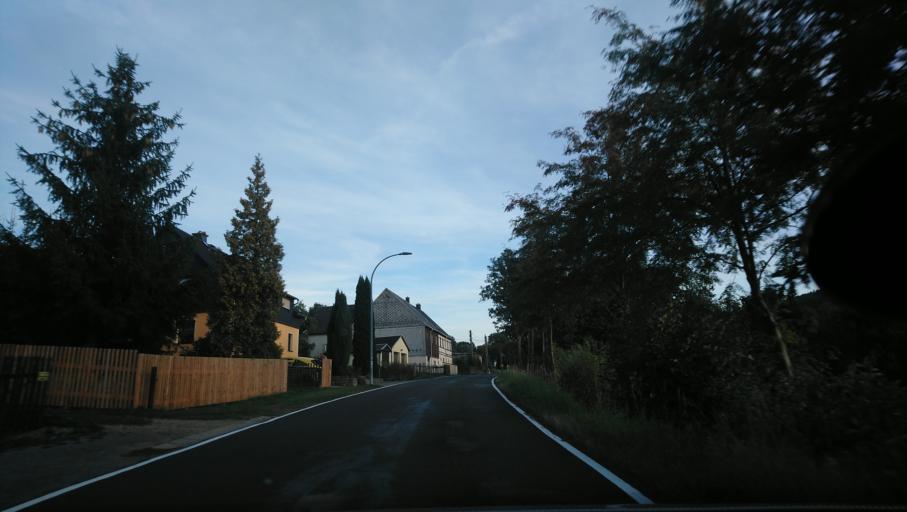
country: DE
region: Saxony
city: Konigswalde
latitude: 50.5396
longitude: 13.0536
